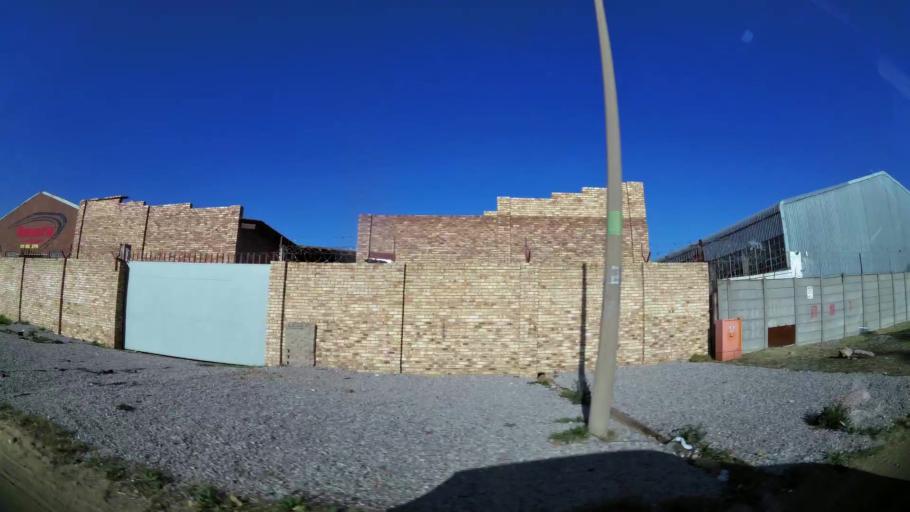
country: ZA
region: Gauteng
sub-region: West Rand District Municipality
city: Randfontein
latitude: -26.2026
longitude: 27.6955
